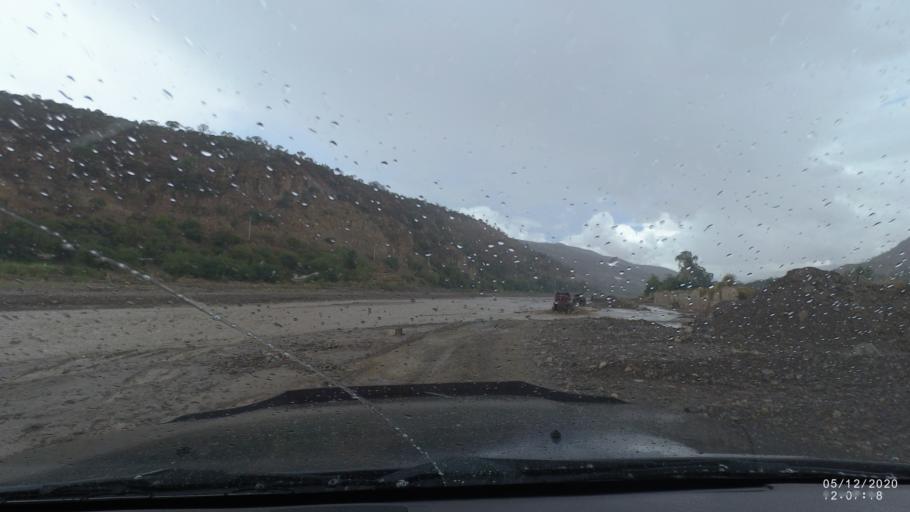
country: BO
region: Cochabamba
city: Sipe Sipe
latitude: -17.5722
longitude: -66.3644
